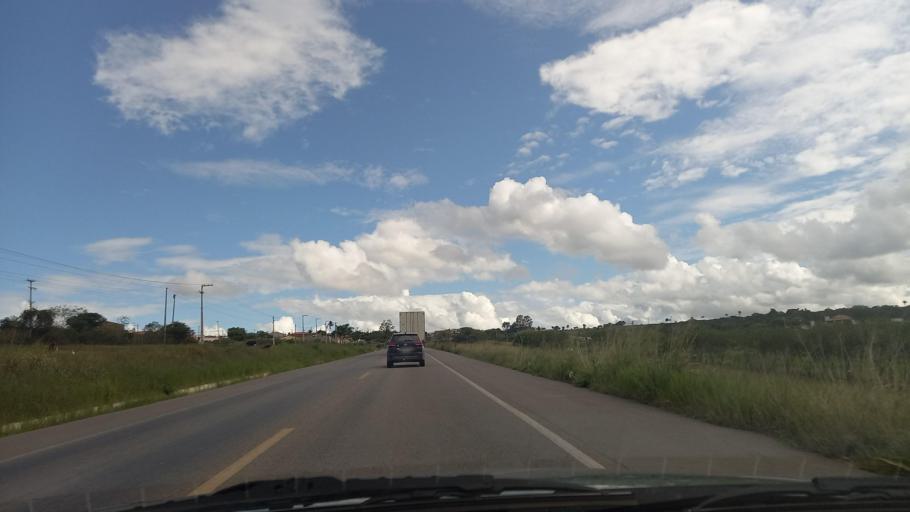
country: BR
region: Pernambuco
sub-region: Lajedo
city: Lajedo
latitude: -8.7019
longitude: -36.4158
